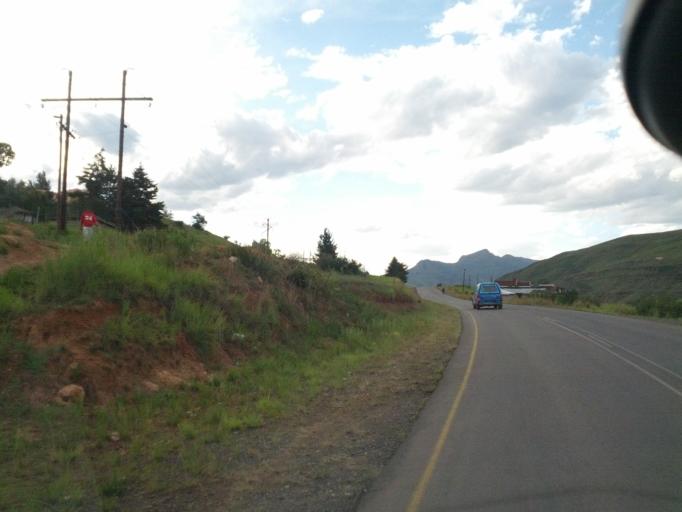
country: LS
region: Qacha's Nek
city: Qacha's Nek
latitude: -30.0960
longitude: 28.6484
